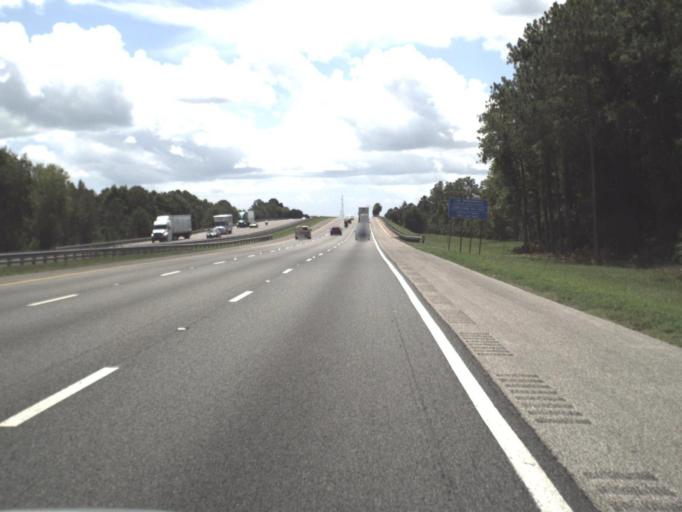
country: US
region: Florida
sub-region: Saint Johns County
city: Butler Beach
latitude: 29.6747
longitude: -81.3096
